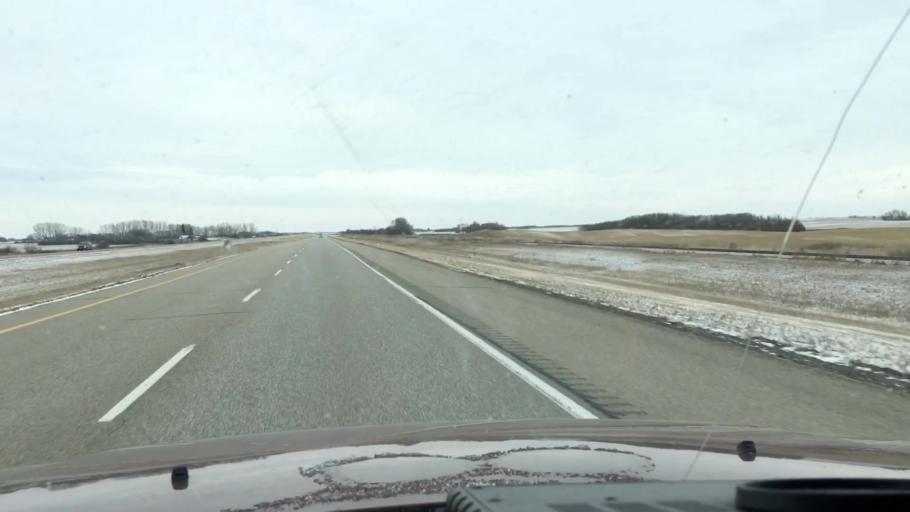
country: CA
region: Saskatchewan
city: Watrous
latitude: 51.3471
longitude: -106.1106
